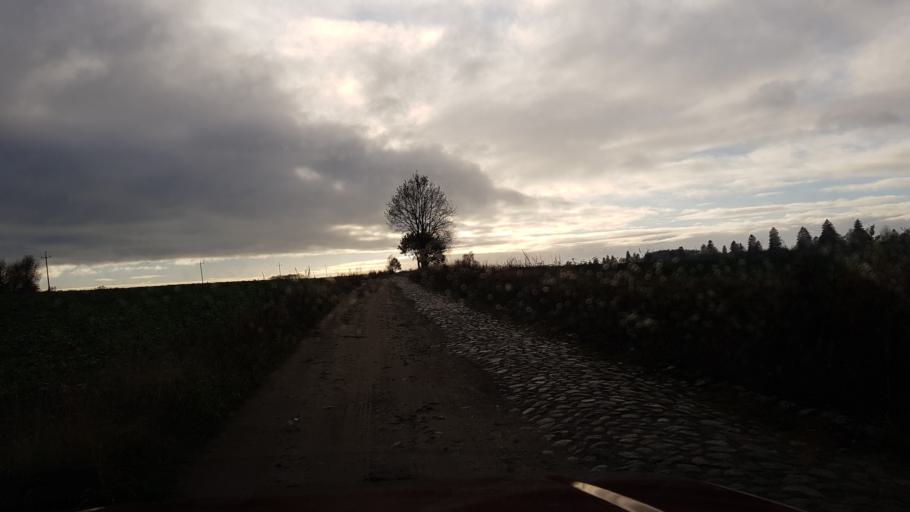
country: PL
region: West Pomeranian Voivodeship
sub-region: Powiat szczecinecki
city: Grzmiaca
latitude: 53.9954
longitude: 16.4173
